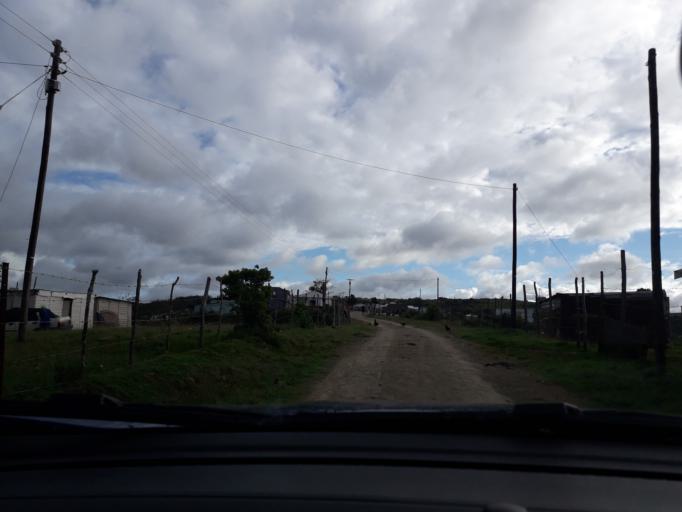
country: ZA
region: Eastern Cape
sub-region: Buffalo City Metropolitan Municipality
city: East London
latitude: -32.8038
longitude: 27.9652
